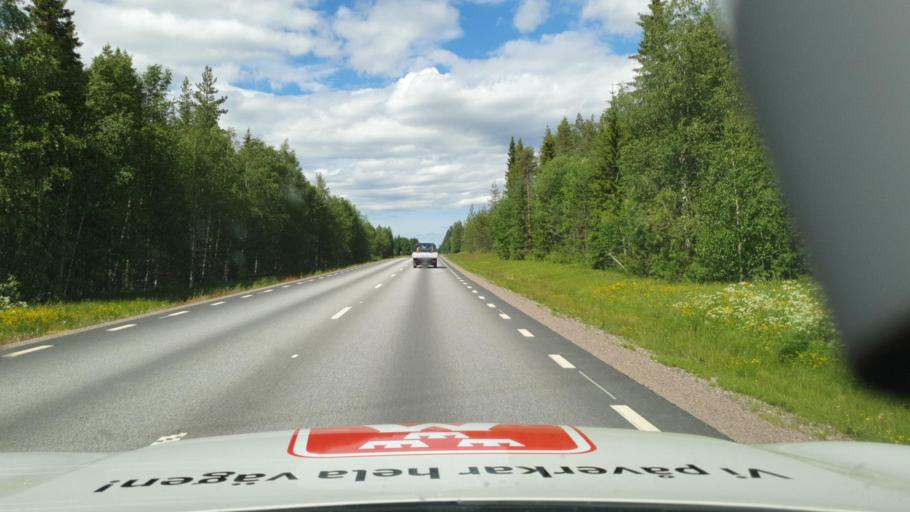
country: SE
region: Vaesterbotten
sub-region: Skelleftea Kommun
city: Langsele
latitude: 65.0993
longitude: 19.9824
